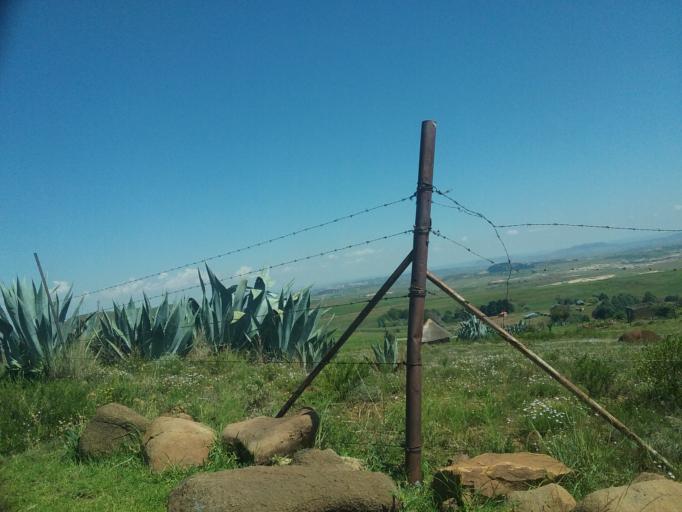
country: LS
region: Berea
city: Teyateyaneng
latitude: -29.2173
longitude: 27.8672
